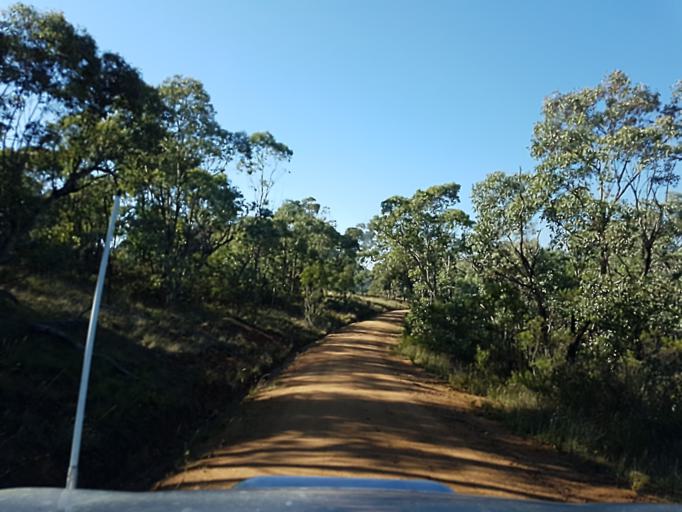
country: AU
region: New South Wales
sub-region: Snowy River
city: Jindabyne
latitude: -36.9384
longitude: 148.3388
